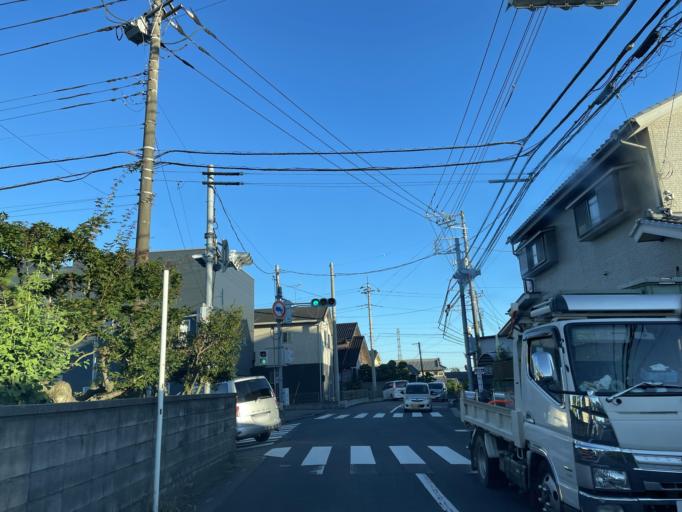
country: JP
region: Saitama
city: Hanno
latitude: 35.8264
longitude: 139.3627
